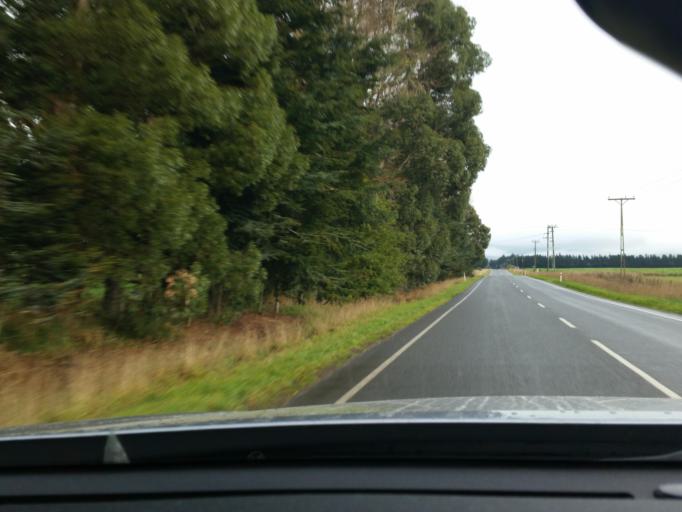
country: NZ
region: Southland
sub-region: Southland District
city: Winton
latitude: -45.8857
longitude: 168.3553
